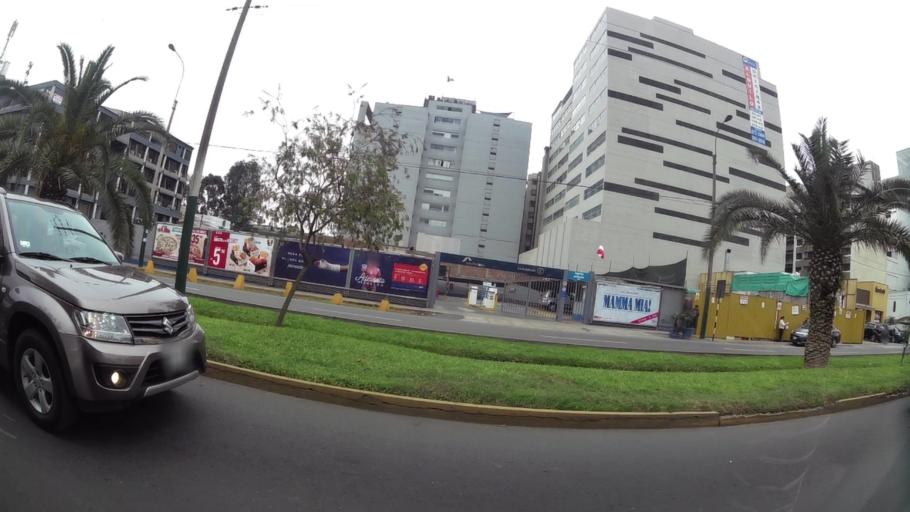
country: PE
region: Lima
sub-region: Lima
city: La Molina
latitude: -12.1007
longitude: -76.9697
